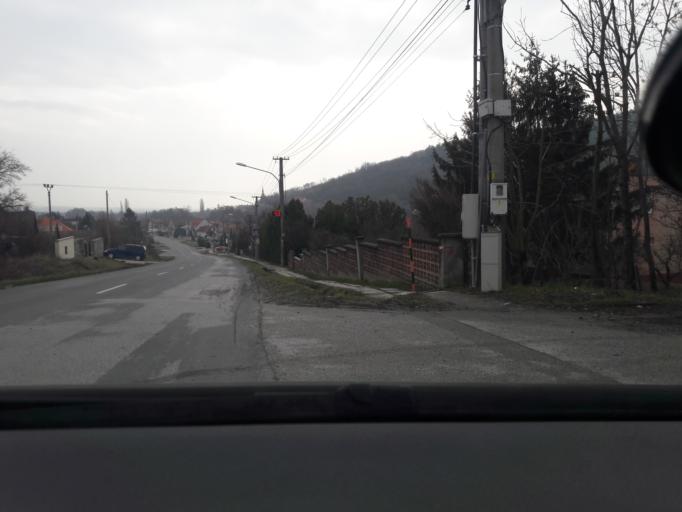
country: SK
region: Trnavsky
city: Smolenice
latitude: 48.4743
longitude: 17.4329
